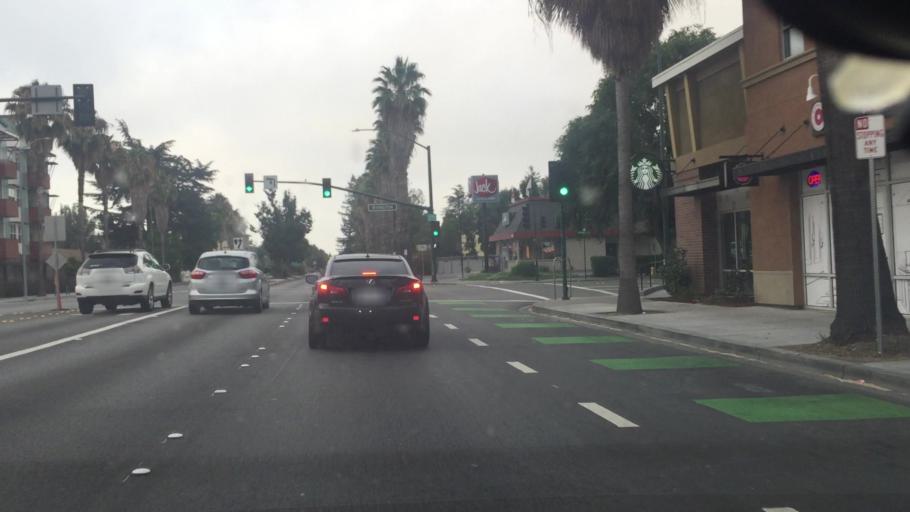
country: US
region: California
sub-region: Alameda County
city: Fremont
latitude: 37.5315
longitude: -121.9590
